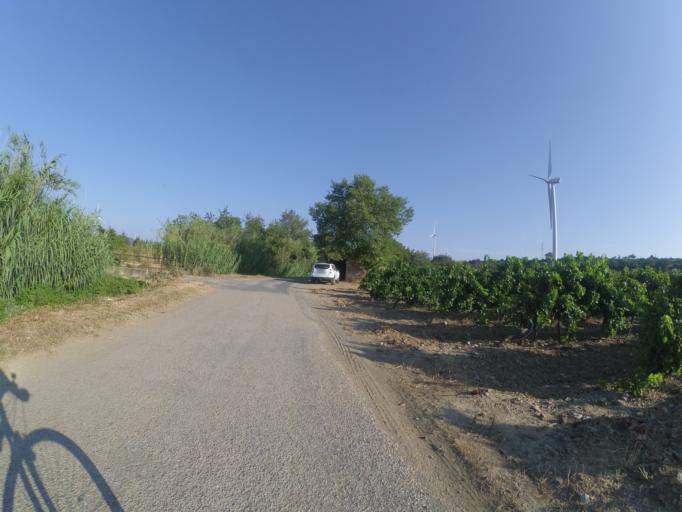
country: FR
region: Languedoc-Roussillon
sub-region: Departement des Pyrenees-Orientales
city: Pezilla-la-Riviere
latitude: 42.7138
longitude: 2.7693
